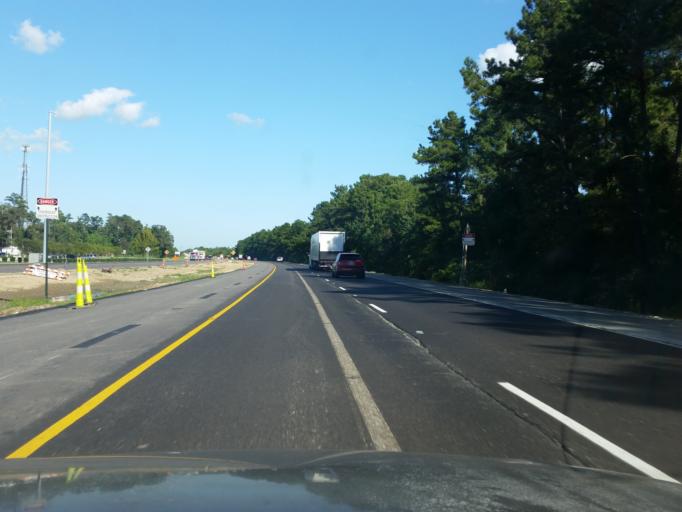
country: US
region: Louisiana
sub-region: Saint Tammany Parish
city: Slidell
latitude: 30.2987
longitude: -89.7144
